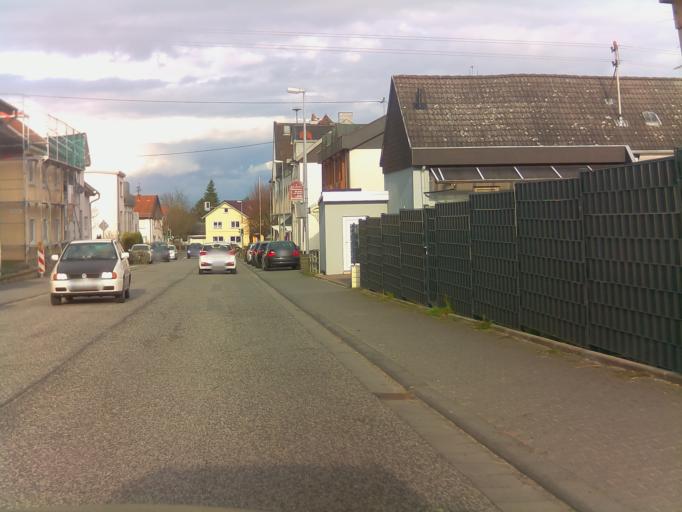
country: DE
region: Rheinland-Pfalz
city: Weiler
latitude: 49.9550
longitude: 7.8636
